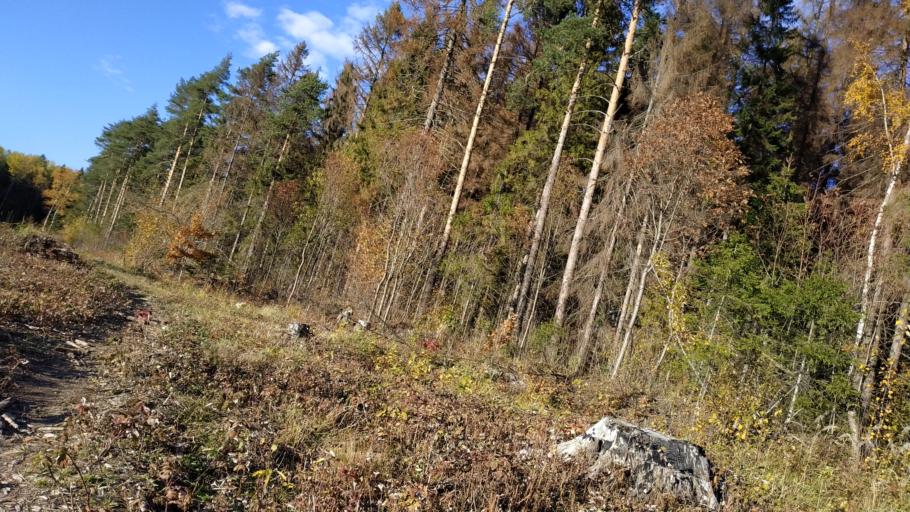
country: RU
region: Moskovskaya
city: Lobnya
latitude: 55.9990
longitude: 37.4622
